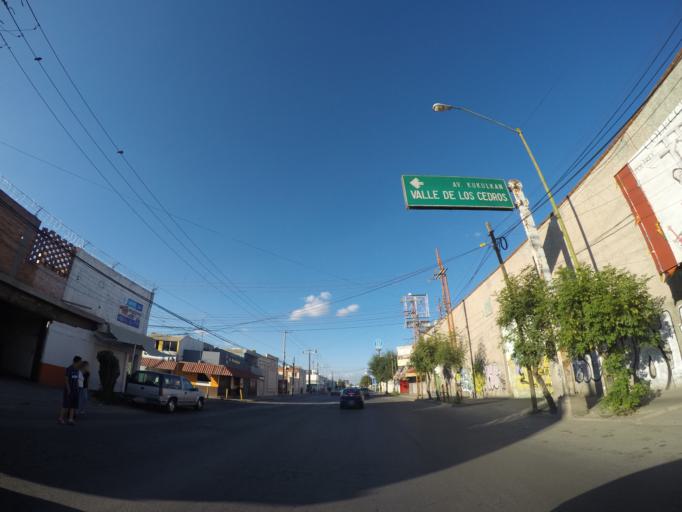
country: MX
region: San Luis Potosi
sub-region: San Luis Potosi
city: San Luis Potosi
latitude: 22.1728
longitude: -101.0000
